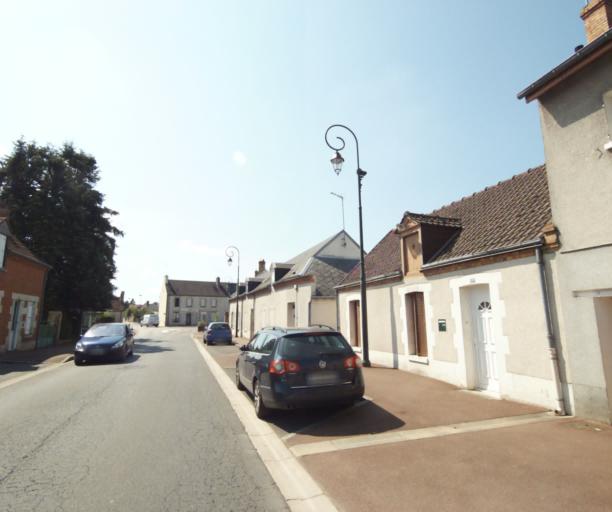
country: FR
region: Centre
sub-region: Departement du Loiret
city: Saint-Cyr-en-Val
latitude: 47.8305
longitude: 1.9698
